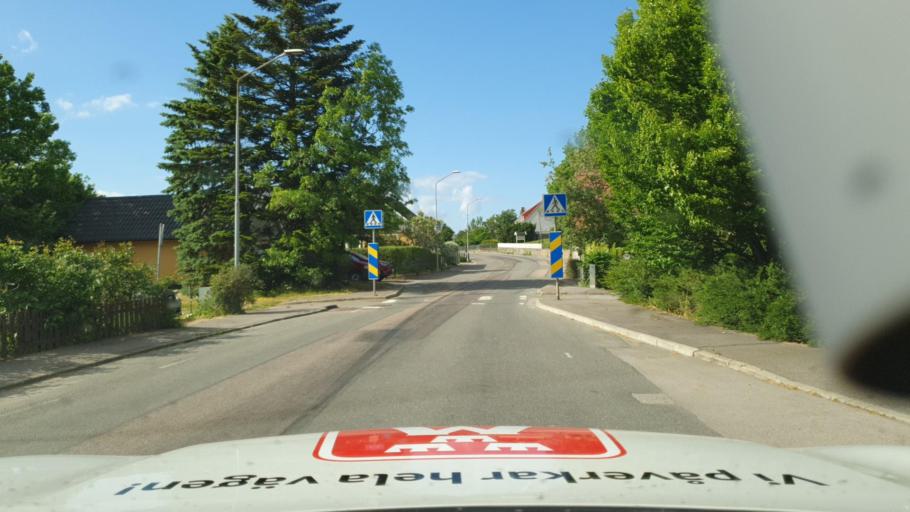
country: SE
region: Skane
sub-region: Simrishamns Kommun
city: Simrishamn
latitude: 55.5544
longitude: 14.3144
